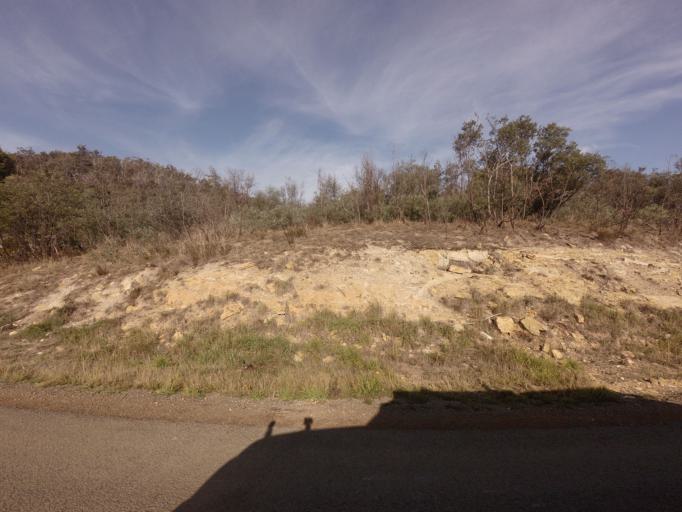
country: AU
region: Tasmania
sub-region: Brighton
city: Bridgewater
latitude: -42.5136
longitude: 147.4177
